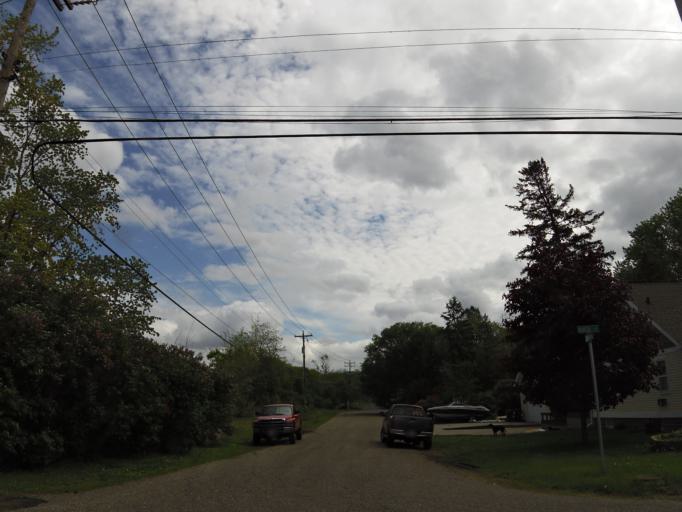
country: US
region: Wisconsin
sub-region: Saint Croix County
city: Hudson
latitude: 44.9831
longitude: -92.7466
